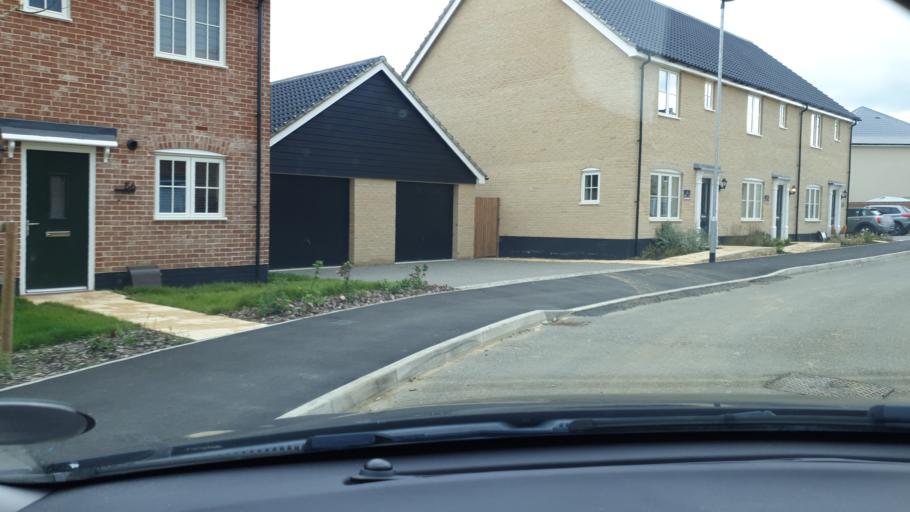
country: GB
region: England
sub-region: Essex
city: Mistley
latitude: 51.9396
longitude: 1.0921
